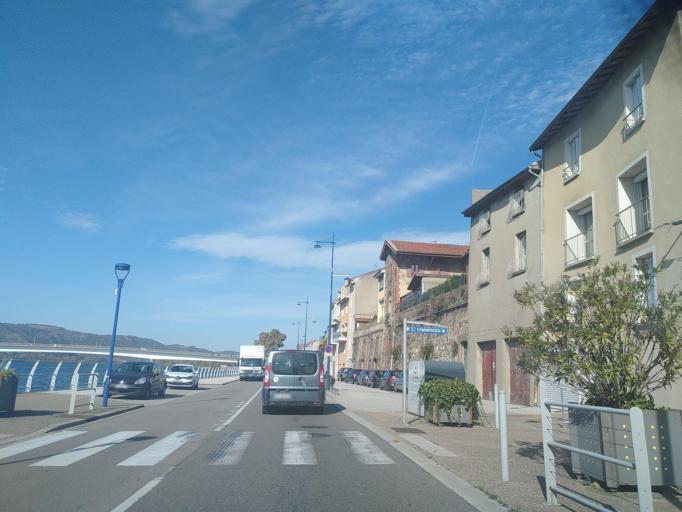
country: FR
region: Rhone-Alpes
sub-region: Departement de la Drome
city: Saint-Vallier
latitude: 45.1813
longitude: 4.8141
